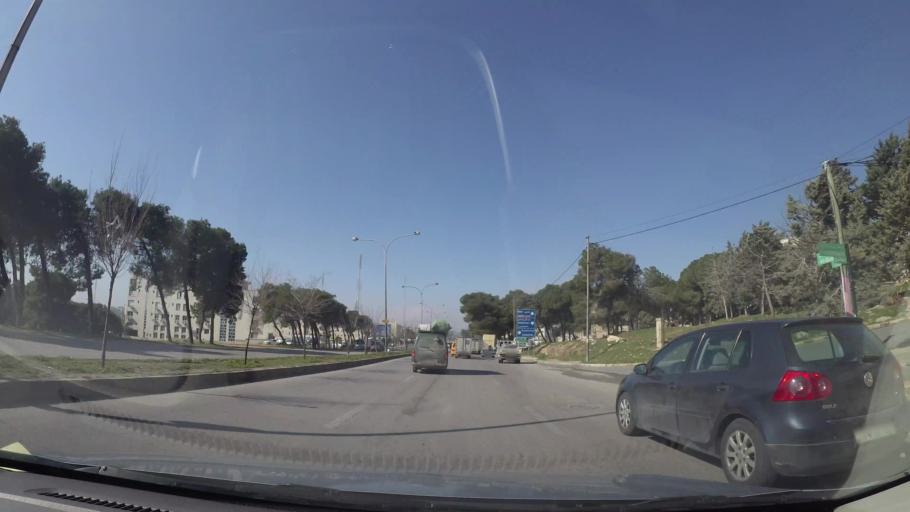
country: JO
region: Amman
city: Al Bunayyat ash Shamaliyah
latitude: 31.9074
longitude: 35.8874
